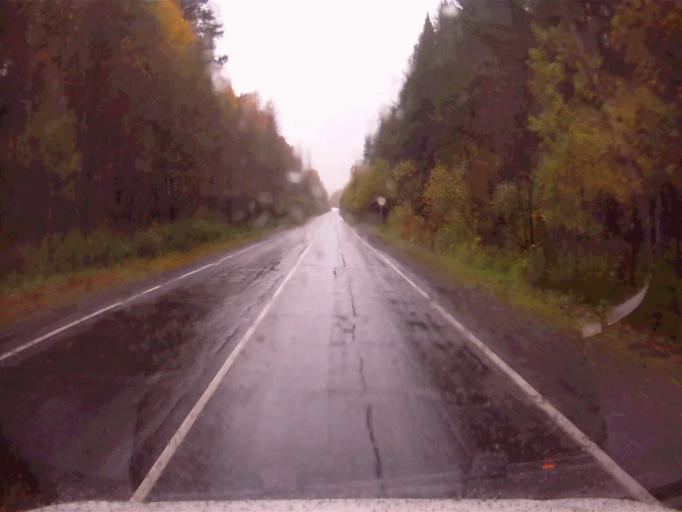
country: RU
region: Chelyabinsk
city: Verkhniy Ufaley
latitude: 55.9374
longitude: 60.4131
